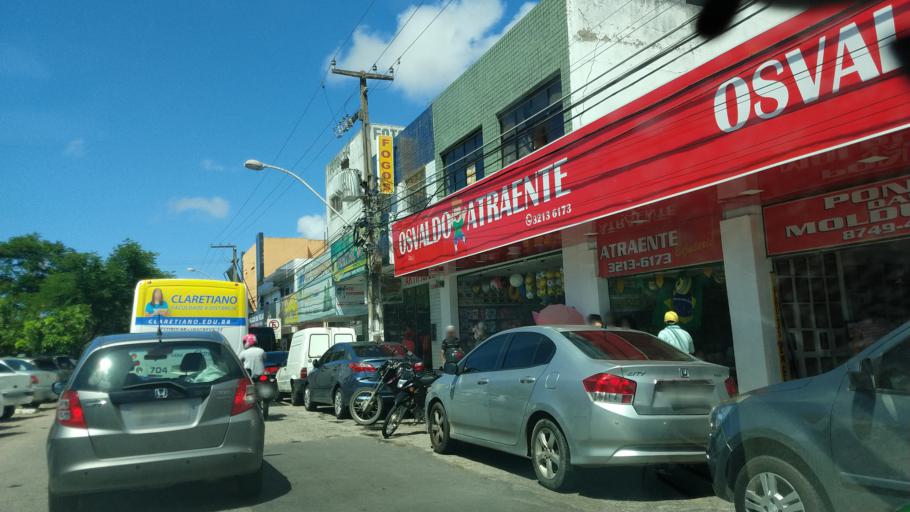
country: BR
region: Rio Grande do Norte
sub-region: Natal
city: Natal
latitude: -5.7988
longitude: -35.2168
